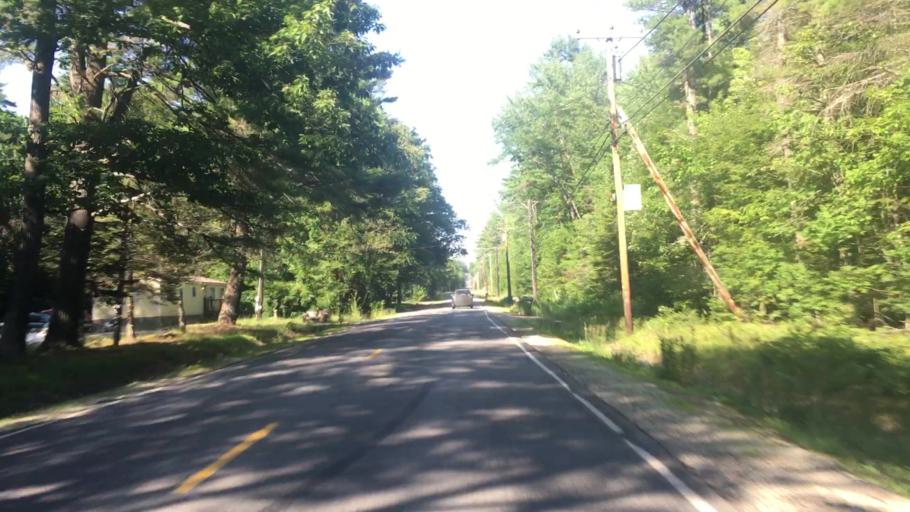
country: US
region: Maine
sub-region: York County
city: Buxton
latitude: 43.6990
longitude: -70.5878
